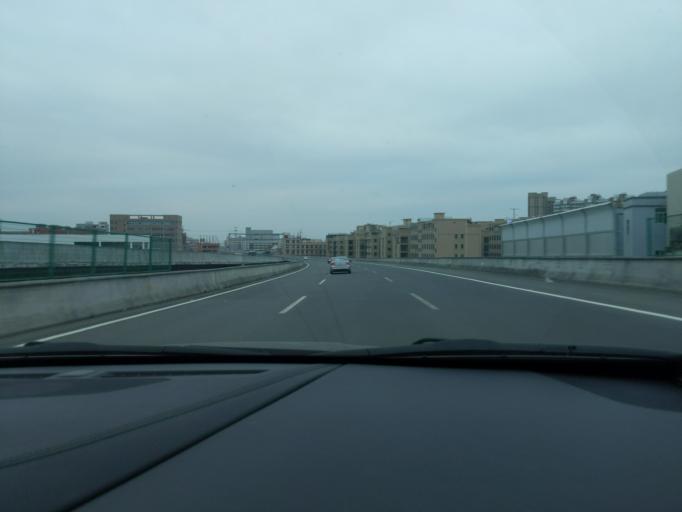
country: CN
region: Fujian
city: Shishi
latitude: 24.7554
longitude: 118.6078
